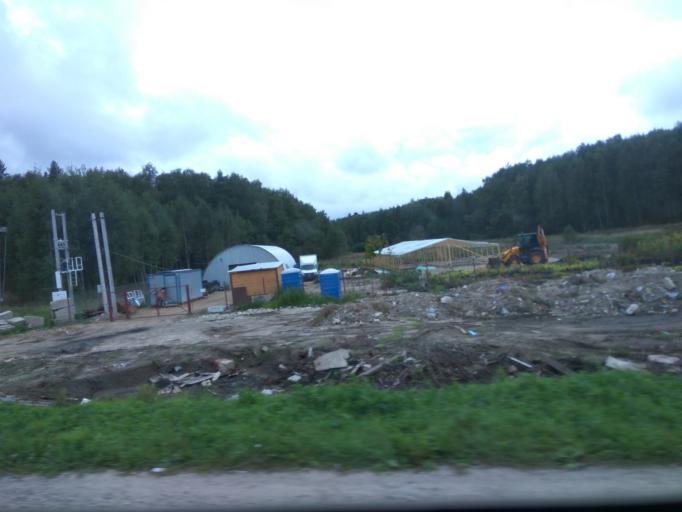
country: RU
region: Moskovskaya
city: Malyshevo
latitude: 55.5189
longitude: 38.3426
